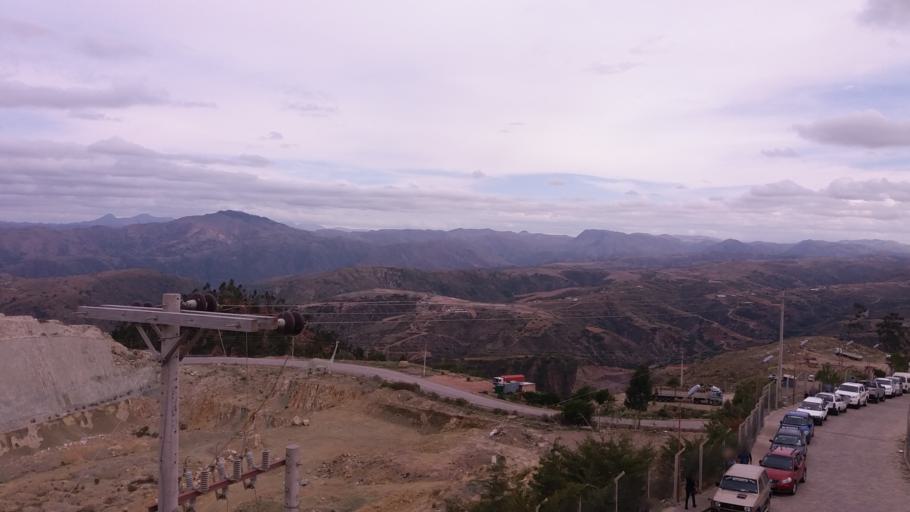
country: BO
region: Chuquisaca
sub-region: Provincia Oropeza
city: Huata
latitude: -19.0069
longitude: -65.2357
